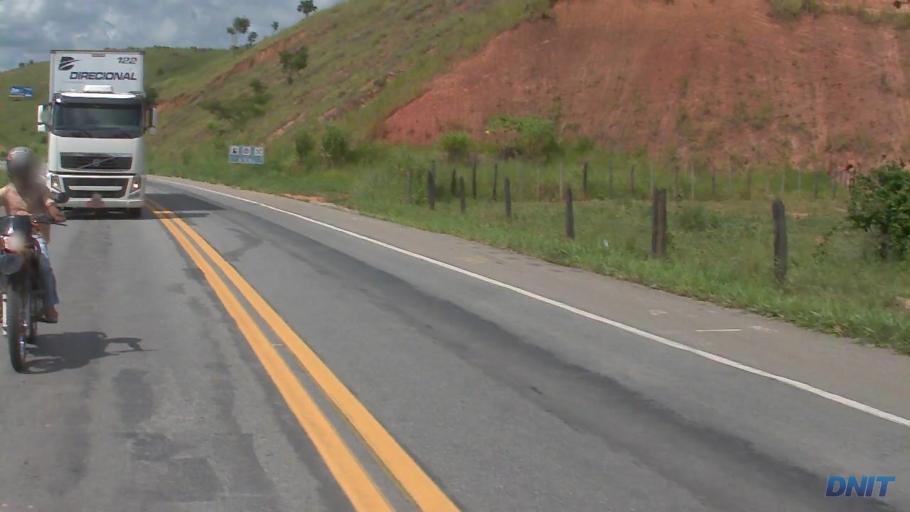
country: BR
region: Minas Gerais
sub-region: Governador Valadares
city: Governador Valadares
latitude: -19.0423
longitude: -42.1499
